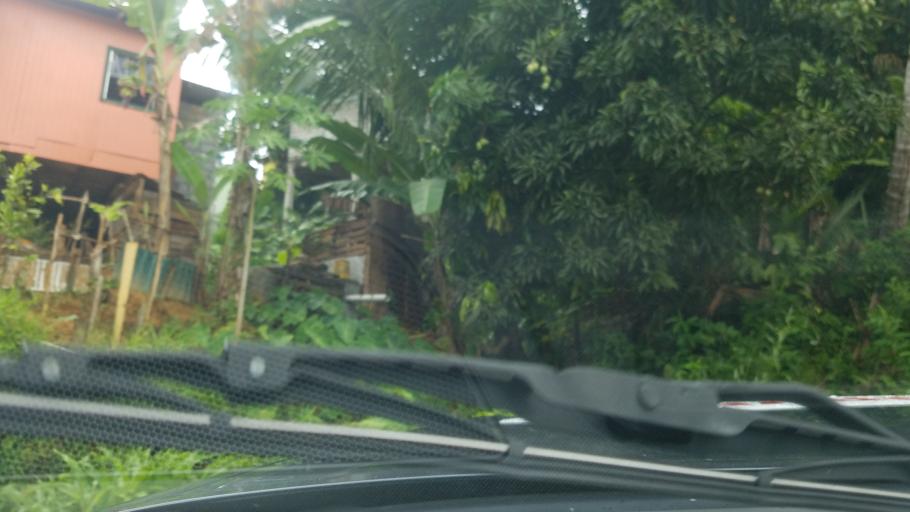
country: LC
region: Castries Quarter
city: Castries
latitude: 13.9880
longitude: -60.9971
